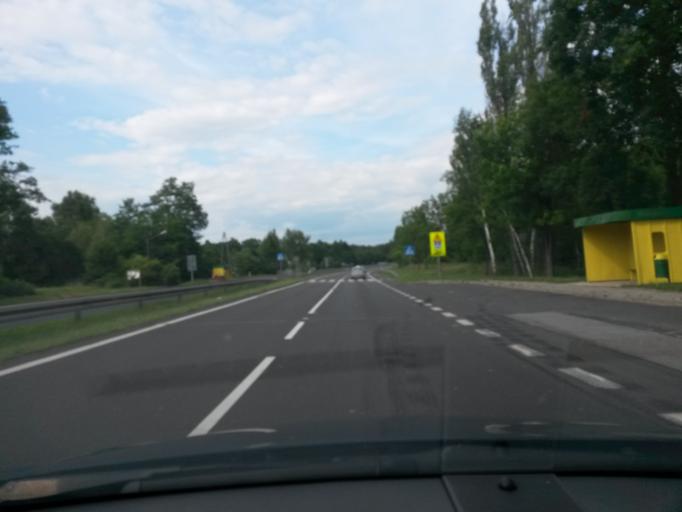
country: PL
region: Lodz Voivodeship
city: Zabia Wola
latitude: 52.0417
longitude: 20.7008
